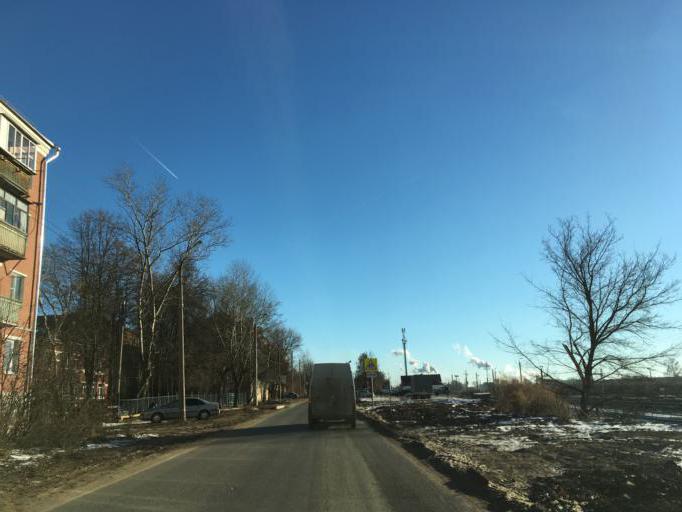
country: RU
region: Tula
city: Tula
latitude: 54.1845
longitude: 37.6923
